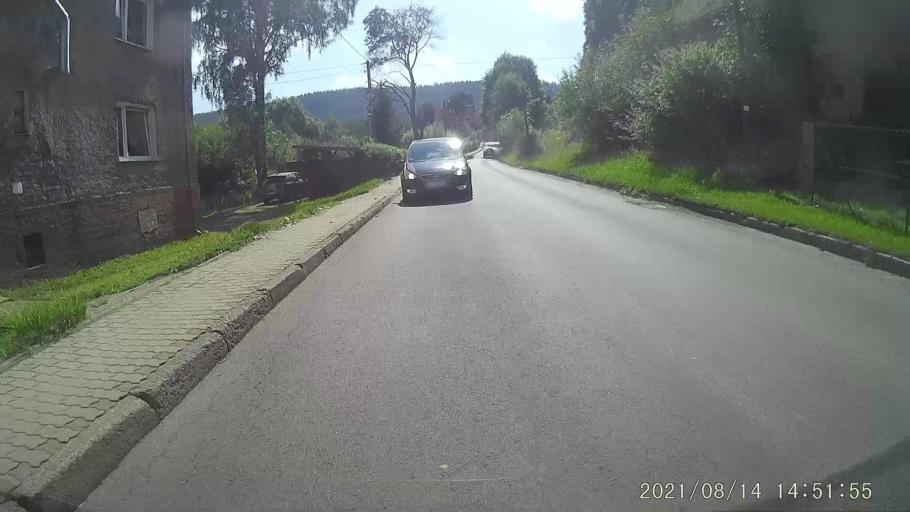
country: PL
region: Lower Silesian Voivodeship
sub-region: Powiat walbrzyski
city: Gluszyca Gorna
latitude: 50.6635
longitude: 16.3754
